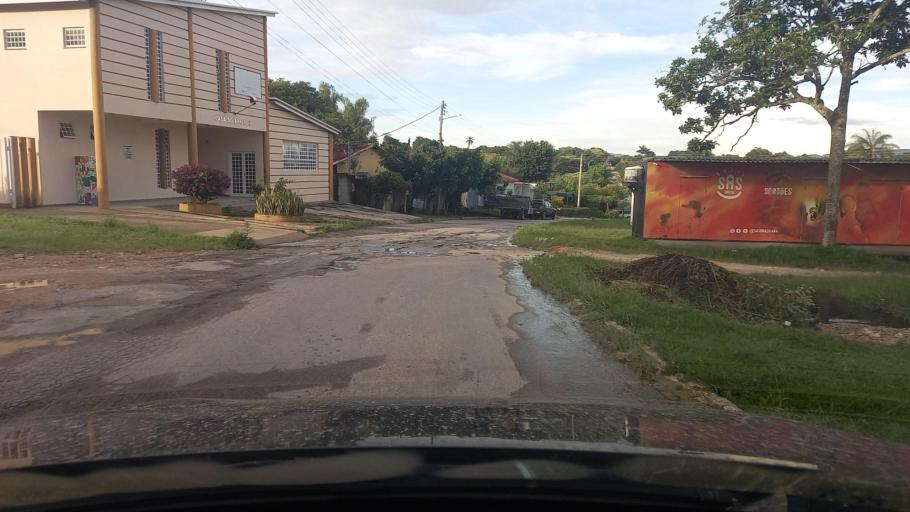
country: BR
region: Goias
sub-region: Cavalcante
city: Cavalcante
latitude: -13.7965
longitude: -47.4613
